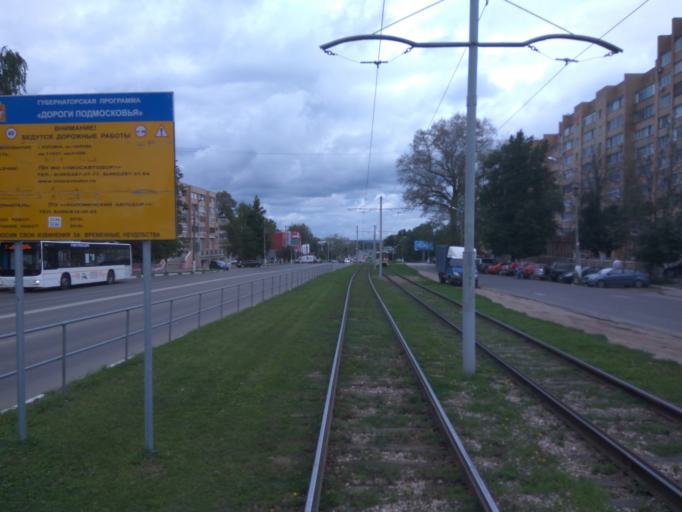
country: RU
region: Moskovskaya
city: Kolomna
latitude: 55.0844
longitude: 38.7640
